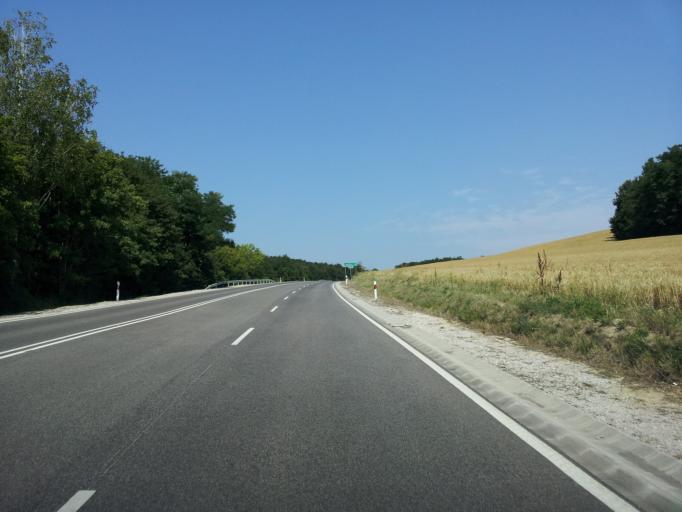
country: HU
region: Zala
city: Pacsa
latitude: 46.8115
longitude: 17.0615
